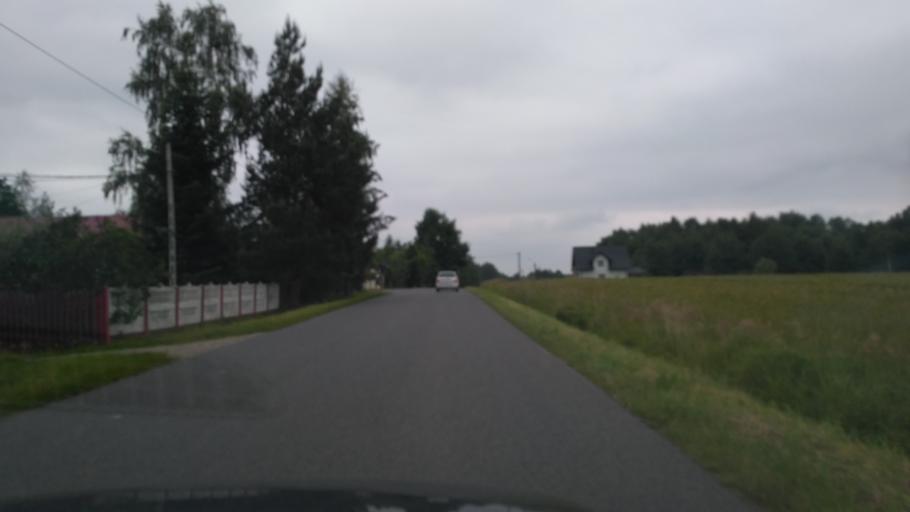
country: PL
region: Subcarpathian Voivodeship
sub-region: Powiat kolbuszowski
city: Niwiska
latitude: 50.1626
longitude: 21.6683
